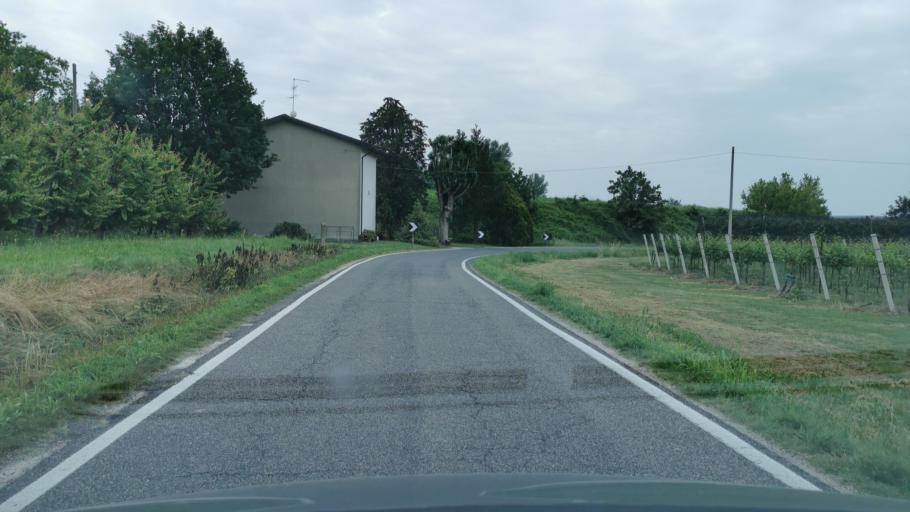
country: IT
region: Emilia-Romagna
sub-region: Provincia di Ravenna
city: Russi
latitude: 44.3859
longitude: 12.0036
